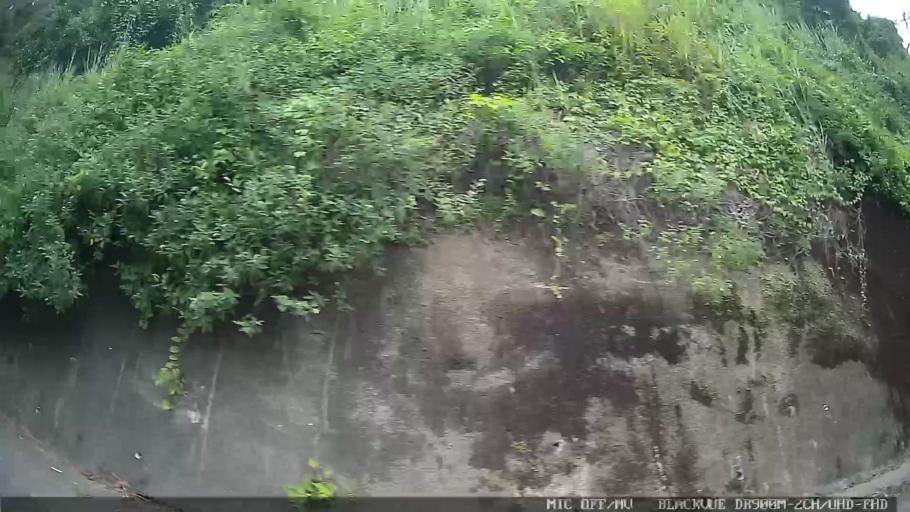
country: BR
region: Sao Paulo
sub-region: Guaruja
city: Guaruja
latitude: -23.9905
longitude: -46.2621
